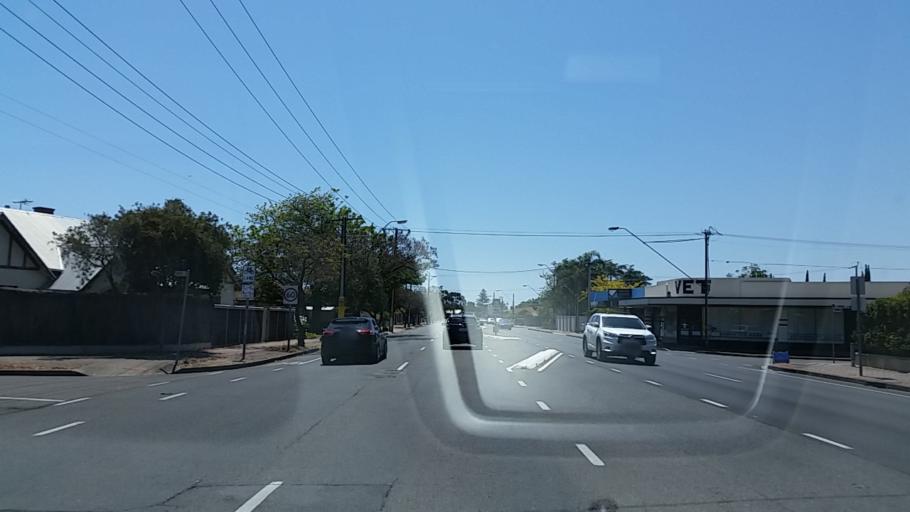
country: AU
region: South Australia
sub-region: Adelaide
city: Glenelg
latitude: -34.9896
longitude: 138.5254
